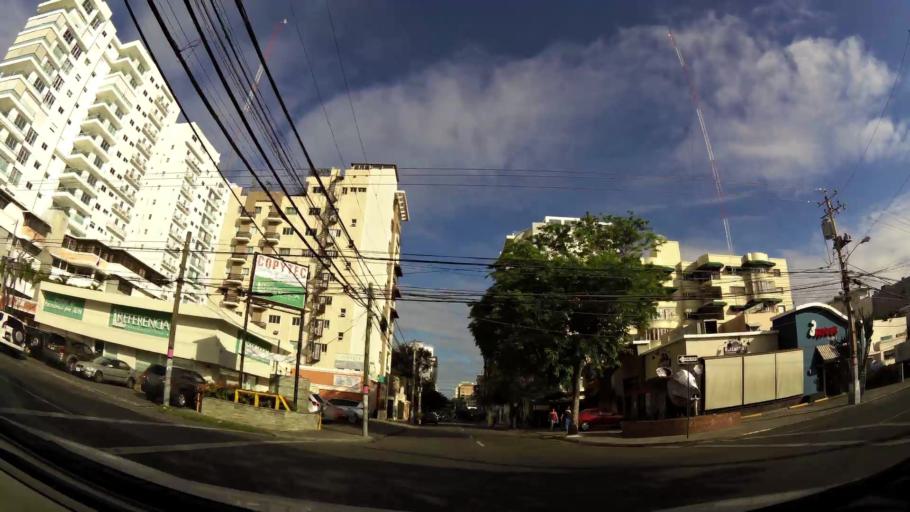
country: DO
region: Nacional
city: La Julia
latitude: 18.4681
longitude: -69.9343
